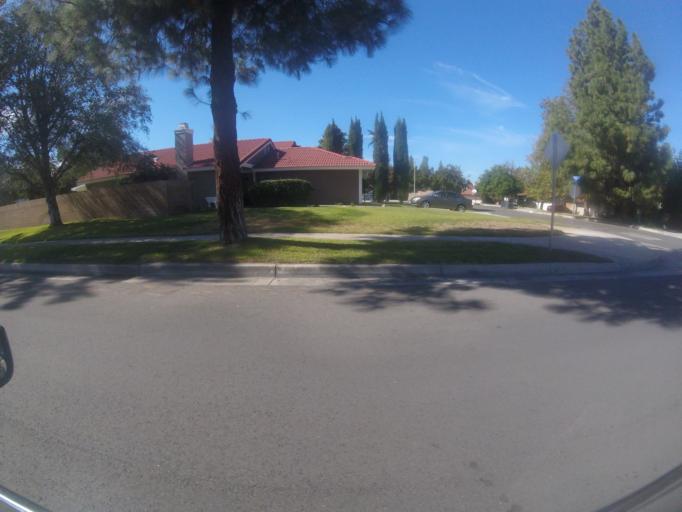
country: US
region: California
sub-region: San Bernardino County
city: Mentone
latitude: 34.0671
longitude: -117.1471
